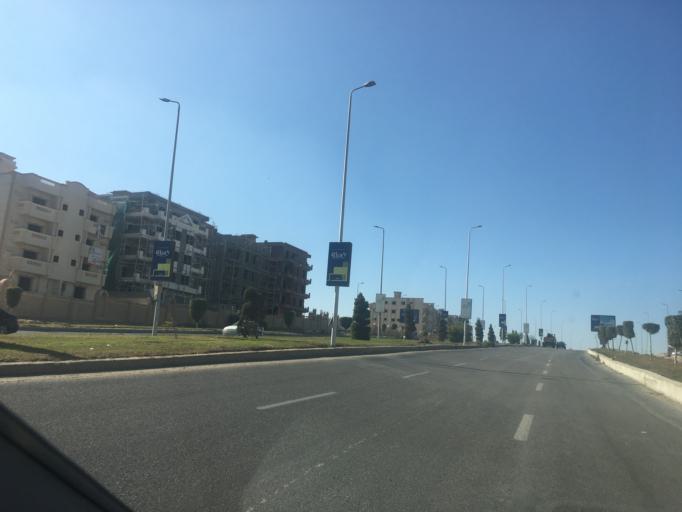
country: EG
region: Al Jizah
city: Awsim
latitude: 30.0199
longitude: 30.9858
